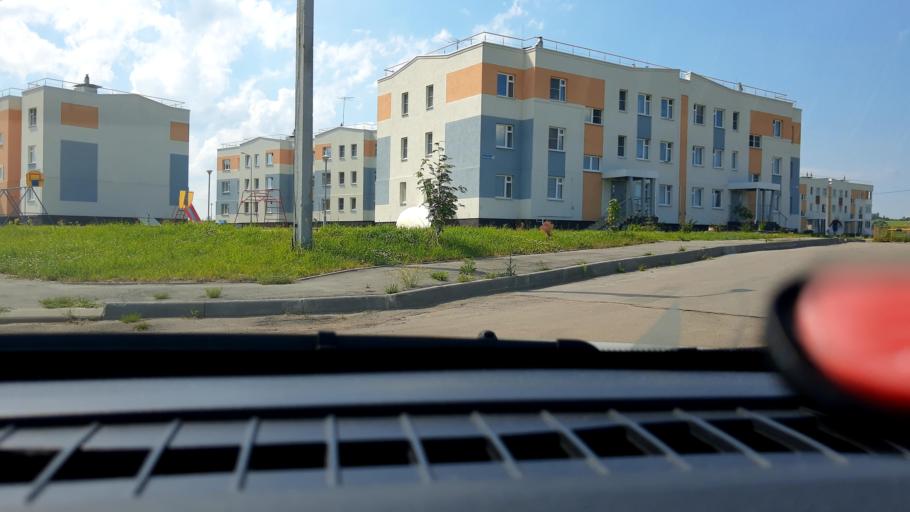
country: RU
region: Nizjnij Novgorod
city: Burevestnik
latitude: 56.1844
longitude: 43.8520
